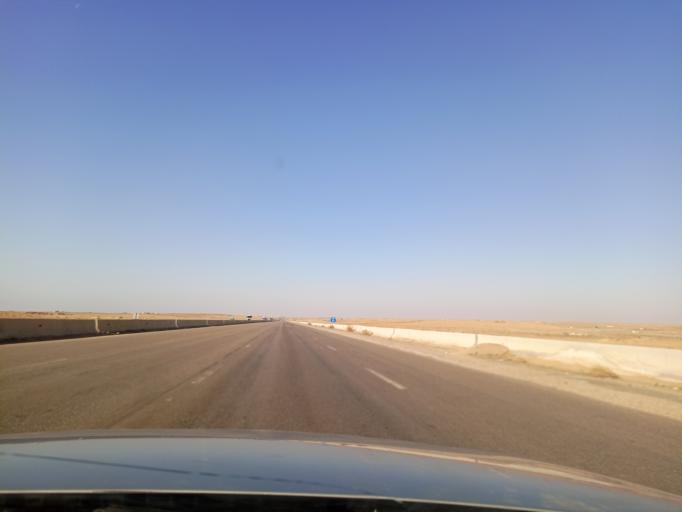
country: EG
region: Muhafazat al Fayyum
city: Tamiyah
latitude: 29.6130
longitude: 30.9249
